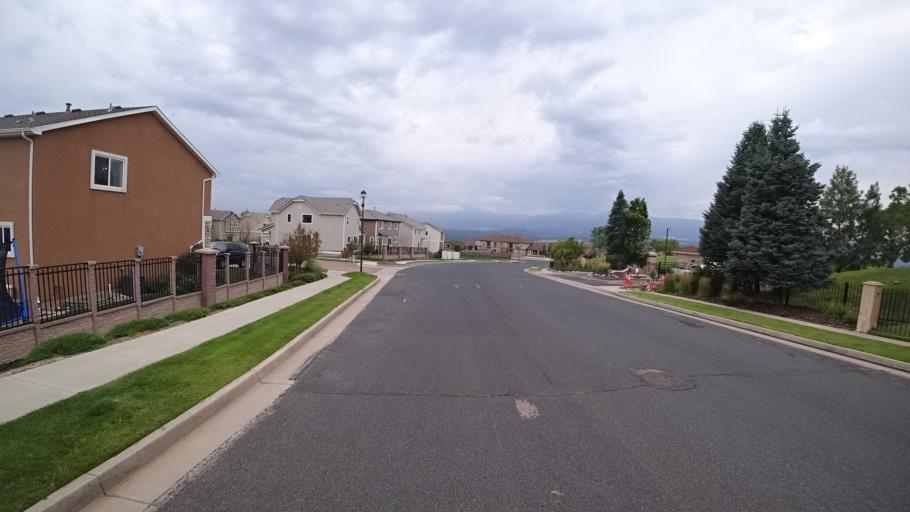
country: US
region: Colorado
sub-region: El Paso County
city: Gleneagle
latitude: 39.0044
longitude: -104.7952
